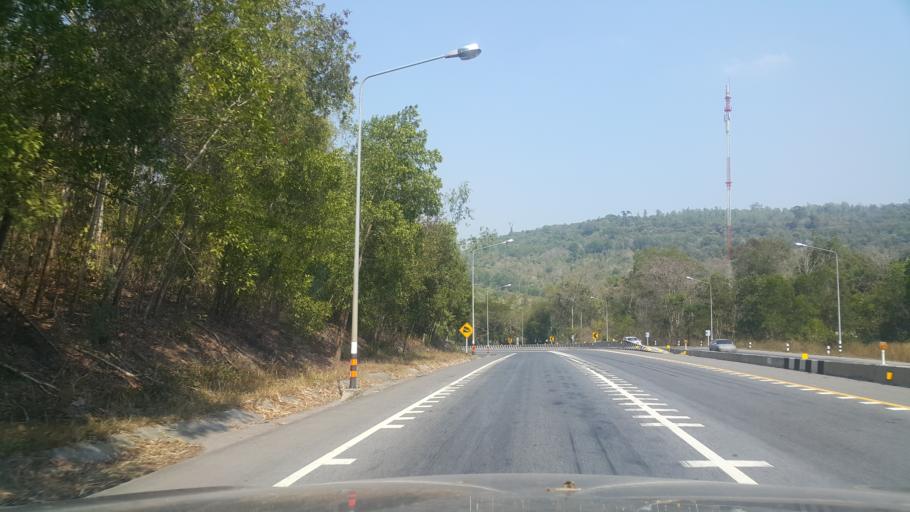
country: TH
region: Nakhon Ratchasima
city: Wang Nam Khiao
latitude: 14.4589
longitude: 101.9041
